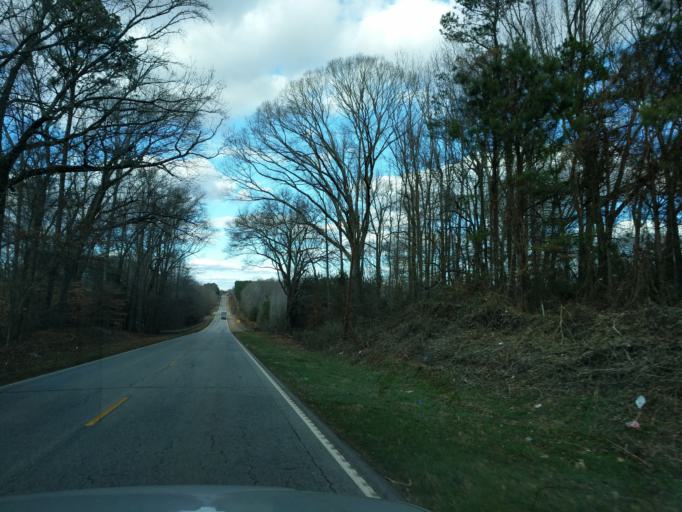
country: US
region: South Carolina
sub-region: Laurens County
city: Watts Mills
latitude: 34.6096
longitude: -81.9833
